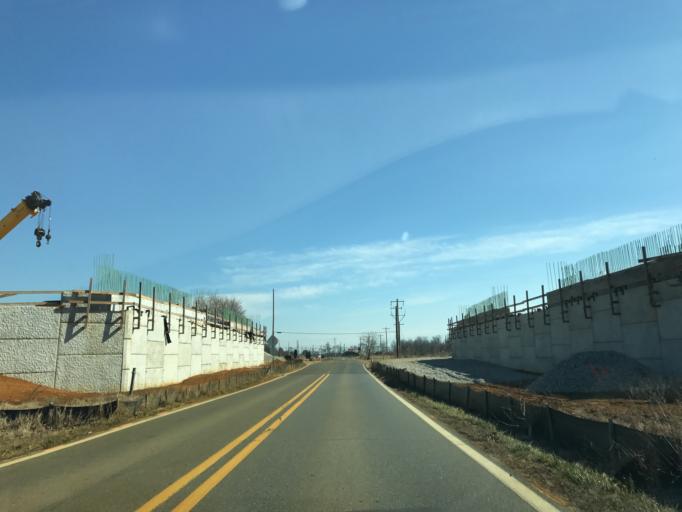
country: US
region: Delaware
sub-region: New Castle County
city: Middletown
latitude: 39.4807
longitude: -75.7247
